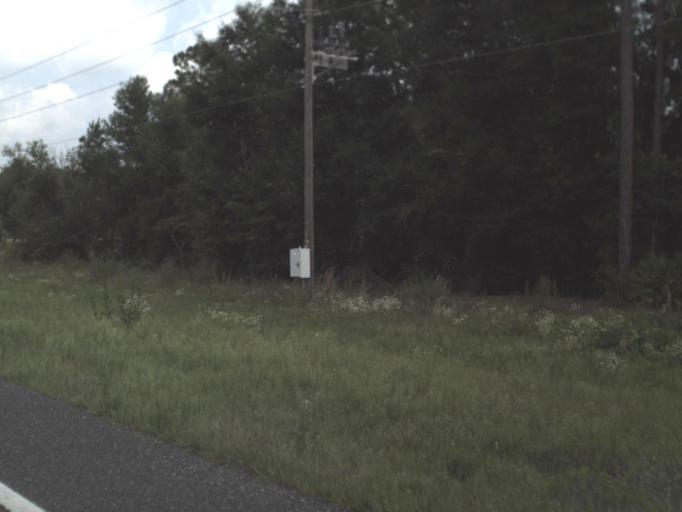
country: US
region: Florida
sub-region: Levy County
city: Bronson
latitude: 29.4349
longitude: -82.6129
